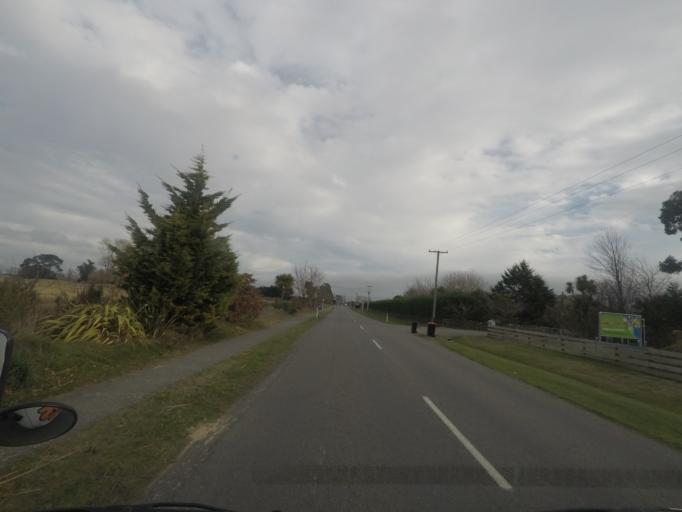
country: NZ
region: Canterbury
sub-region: Waimakariri District
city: Woodend
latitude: -43.2884
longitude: 172.7060
